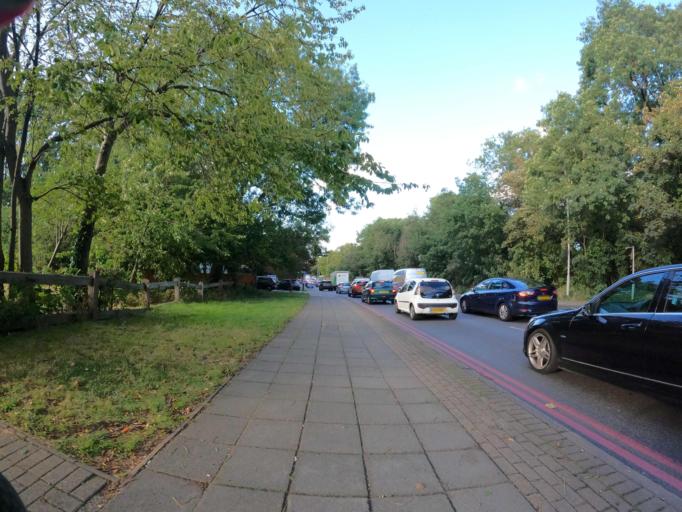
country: GB
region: England
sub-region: Greater London
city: Ealing Broadway
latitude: 51.5255
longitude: -0.2923
